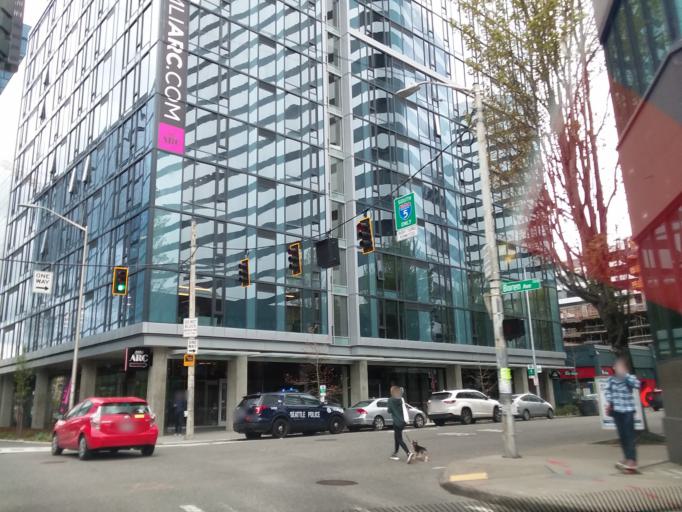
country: US
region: Washington
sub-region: King County
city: Seattle
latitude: 47.6161
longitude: -122.3312
